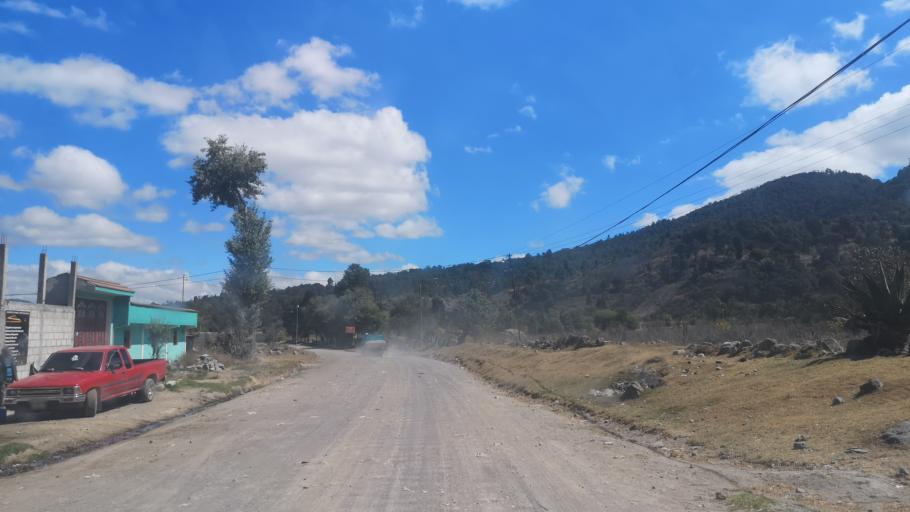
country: GT
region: Quetzaltenango
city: Quetzaltenango
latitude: 14.8049
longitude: -91.5361
